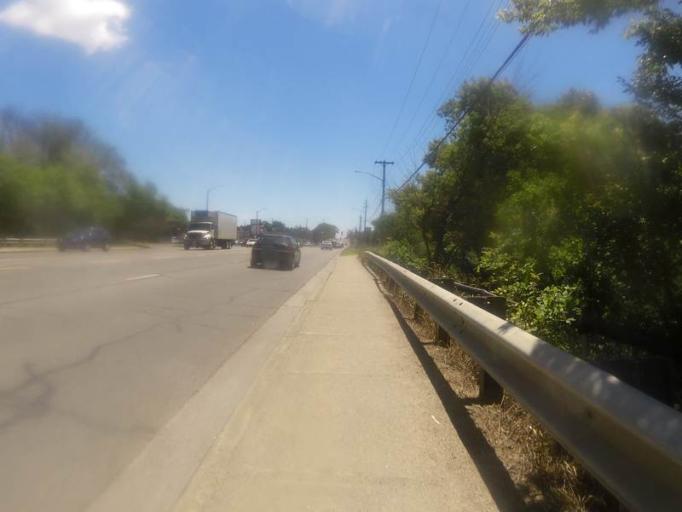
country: CA
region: Ontario
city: Kingston
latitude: 44.2521
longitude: -76.5350
